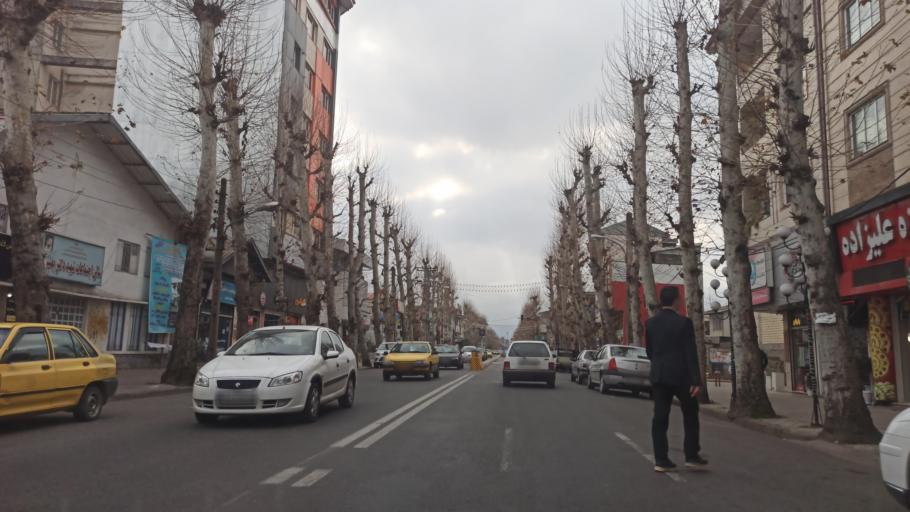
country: IR
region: Gilan
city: Fuman
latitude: 37.2305
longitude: 49.3171
